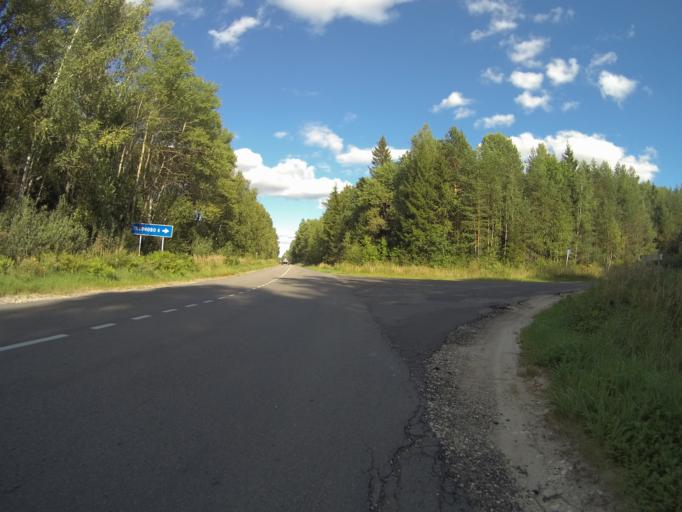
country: RU
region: Vladimir
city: Urshel'skiy
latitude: 55.6072
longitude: 40.2497
